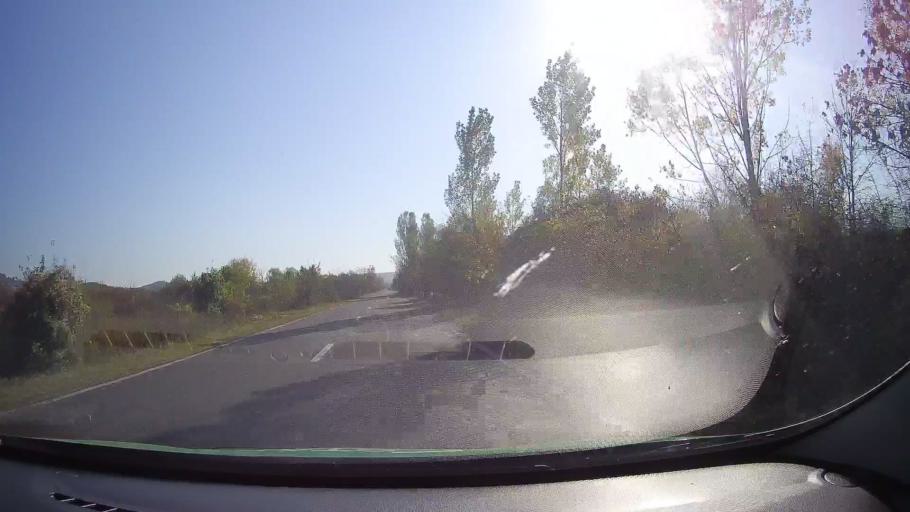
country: RO
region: Timis
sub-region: Comuna Margina
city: Margina
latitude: 45.8524
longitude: 22.2903
